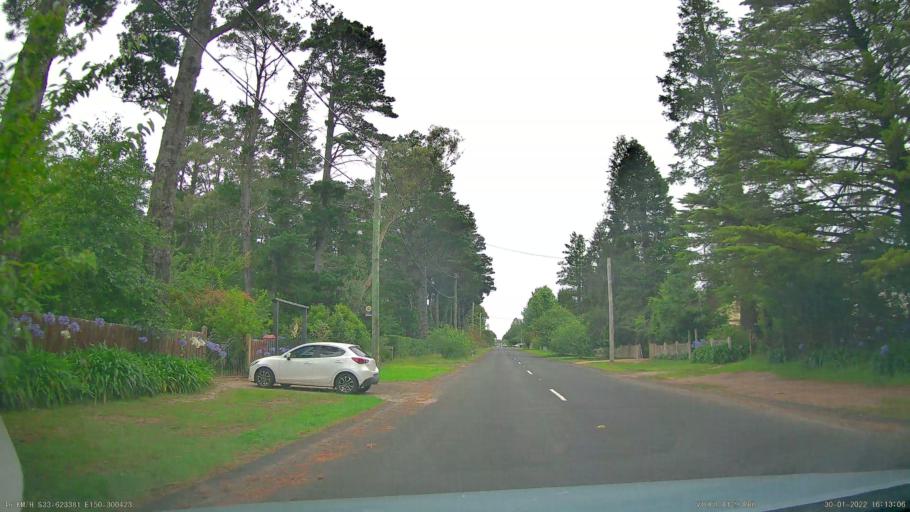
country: AU
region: New South Wales
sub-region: Blue Mountains Municipality
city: Blackheath
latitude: -33.6235
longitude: 150.3003
